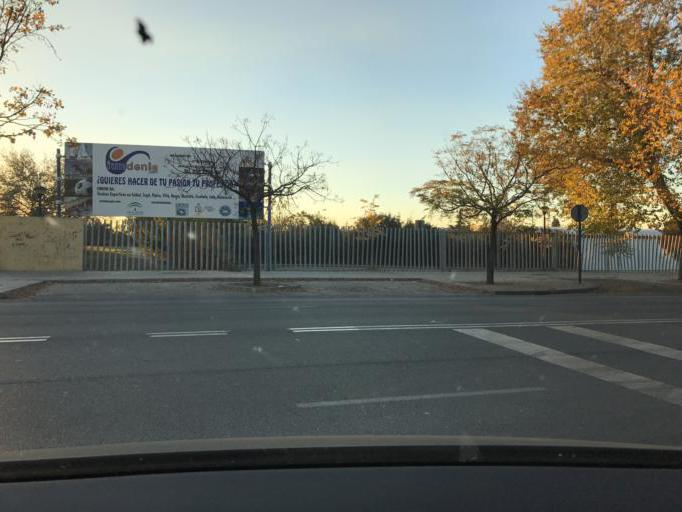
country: ES
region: Andalusia
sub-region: Provincia de Granada
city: Pulianas
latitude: 37.2082
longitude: -3.6094
